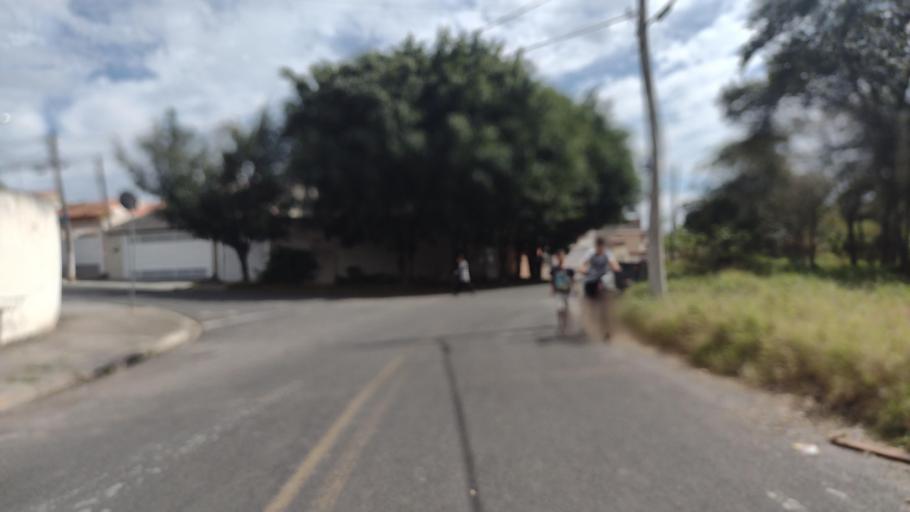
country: BR
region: Sao Paulo
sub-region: Sorocaba
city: Sorocaba
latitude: -23.4240
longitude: -47.4553
